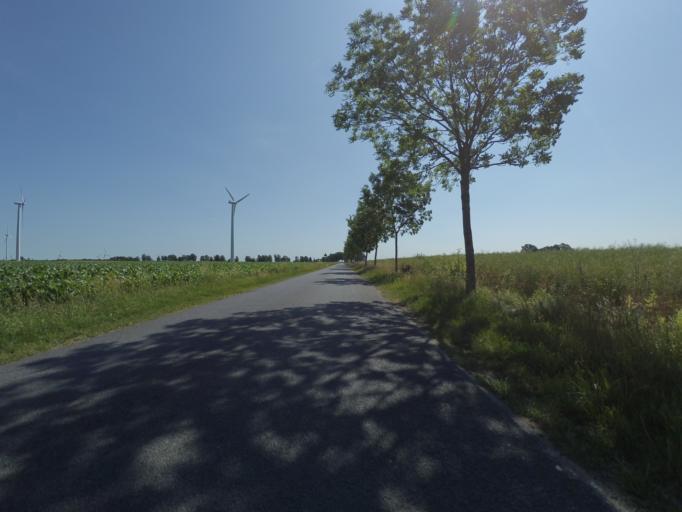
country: DE
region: Brandenburg
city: Pritzwalk
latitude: 53.1176
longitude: 12.1985
